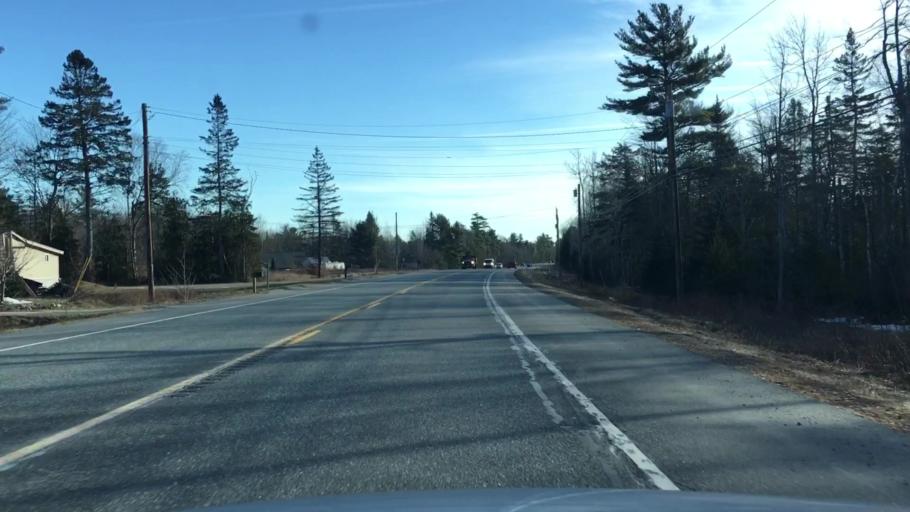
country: US
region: Maine
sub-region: Hancock County
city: Surry
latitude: 44.6128
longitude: -68.5224
